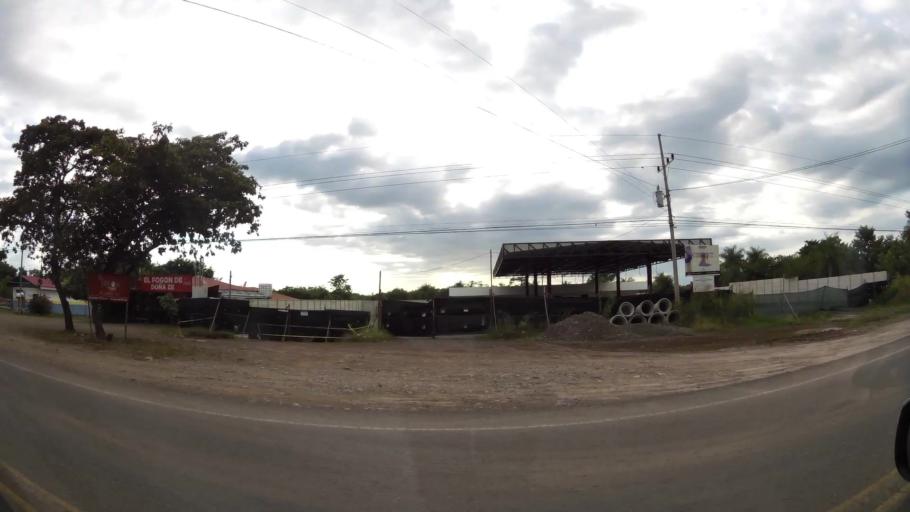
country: CR
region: Alajuela
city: Orotina
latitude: 9.8774
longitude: -84.5749
